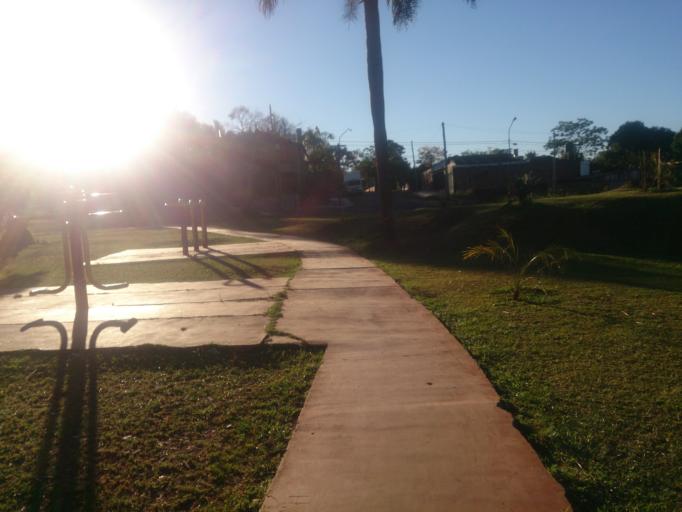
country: AR
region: Misiones
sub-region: Departamento de Obera
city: Obera
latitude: -27.4941
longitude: -55.1204
